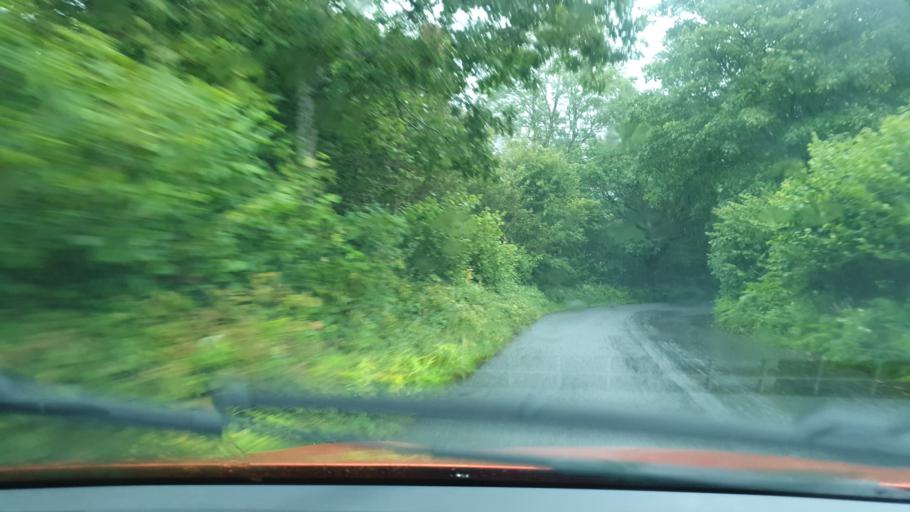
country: GB
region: England
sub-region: Cumbria
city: Millom
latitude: 54.3348
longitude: -3.2378
